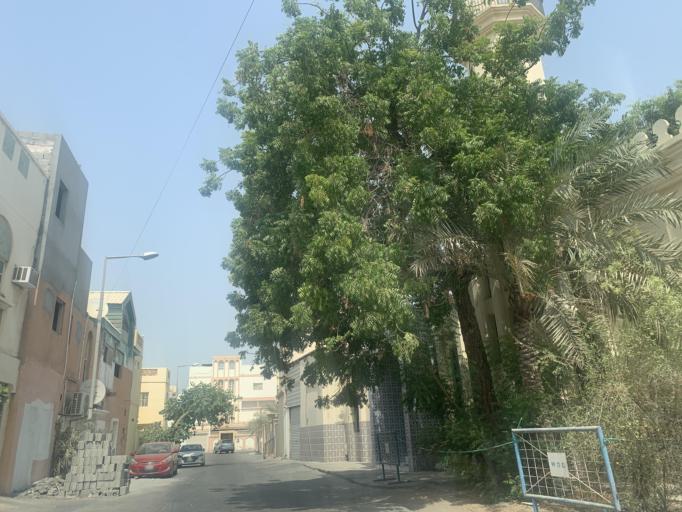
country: BH
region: Manama
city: Jidd Hafs
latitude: 26.2135
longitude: 50.4637
